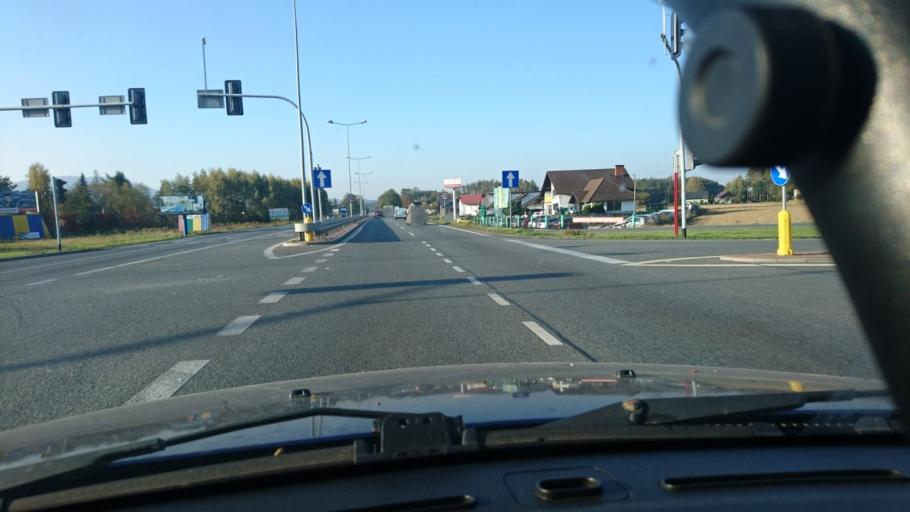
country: PL
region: Silesian Voivodeship
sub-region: Powiat cieszynski
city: Gorki Wielkie
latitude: 49.7583
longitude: 18.8040
